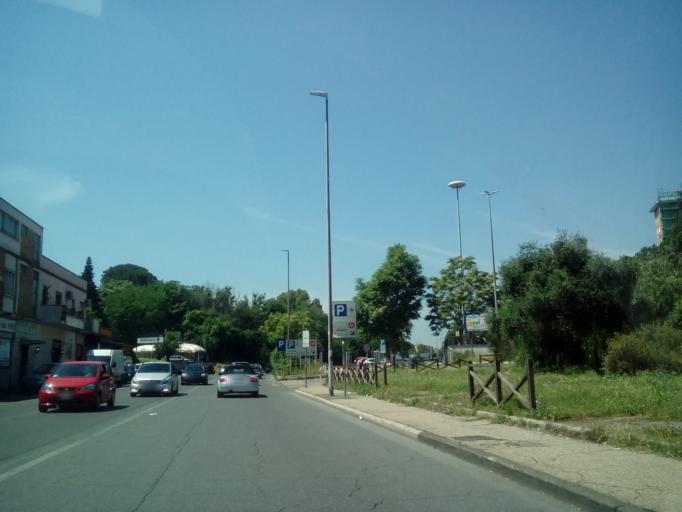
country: IT
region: Latium
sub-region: Citta metropolitana di Roma Capitale
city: Rome
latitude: 41.9152
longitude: 12.5609
